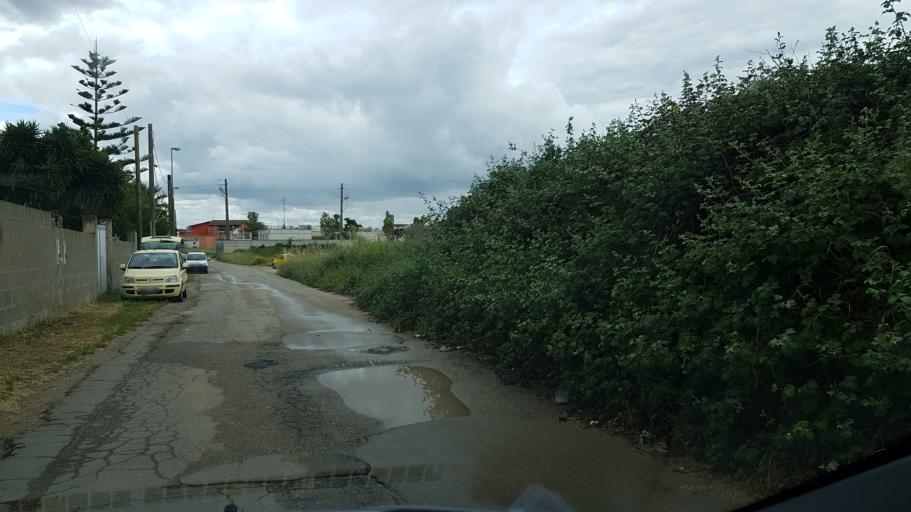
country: IT
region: Apulia
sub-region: Provincia di Brindisi
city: Torchiarolo
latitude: 40.4906
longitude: 18.0464
